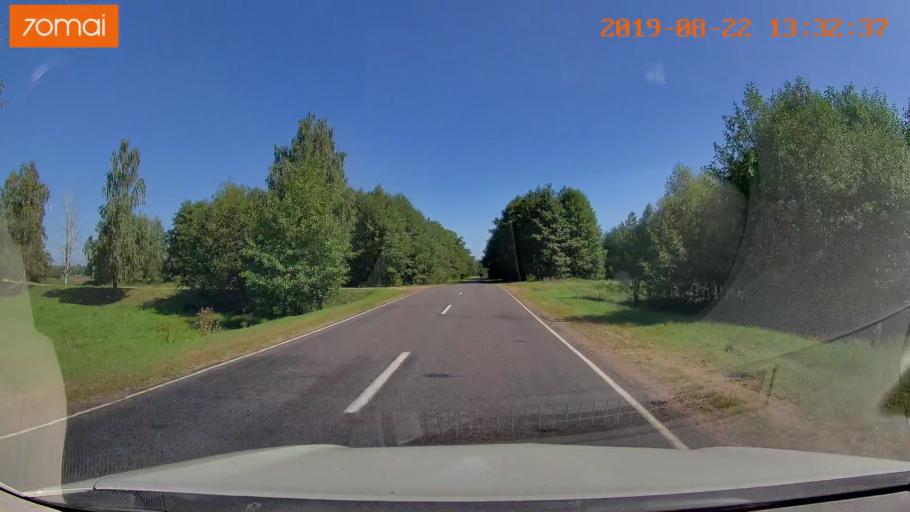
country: BY
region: Minsk
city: Staryya Darohi
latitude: 53.2171
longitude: 28.2082
